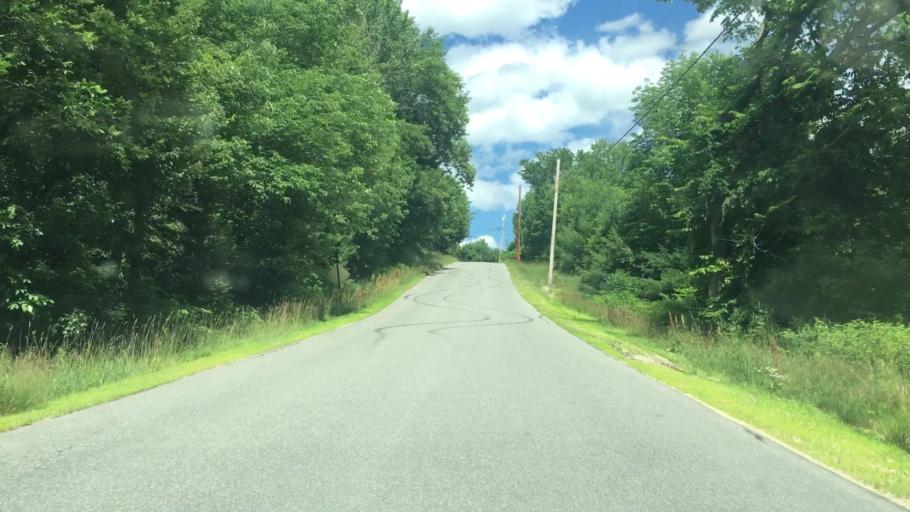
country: US
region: Maine
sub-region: Franklin County
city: Jay
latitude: 44.5357
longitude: -70.2260
